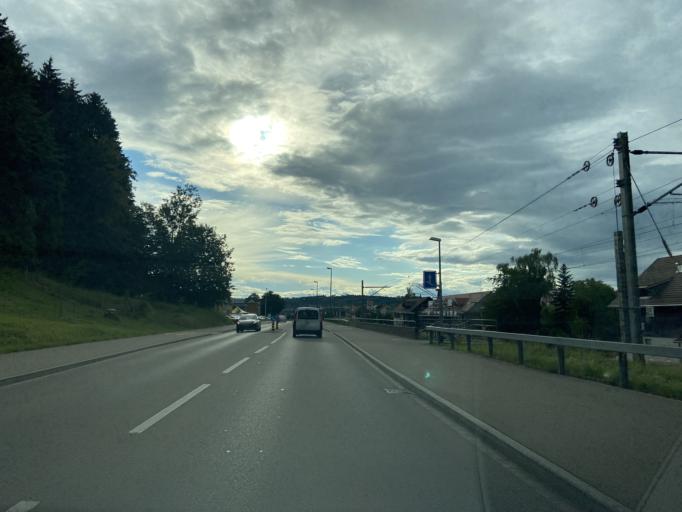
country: CH
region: Zurich
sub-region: Bezirk Winterthur
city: Oberwinterthur (Kreis 2) / Hegi
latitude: 47.5015
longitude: 8.7832
